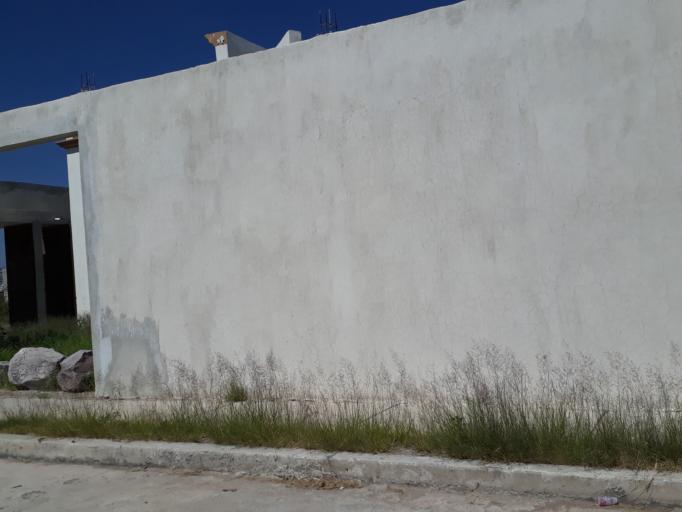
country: MX
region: Aguascalientes
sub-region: Aguascalientes
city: San Sebastian [Fraccionamiento]
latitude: 21.8369
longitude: -102.2964
